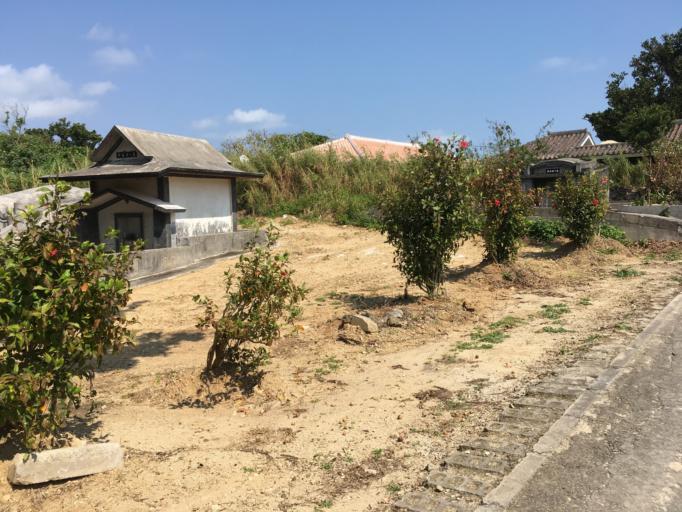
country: JP
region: Okinawa
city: Ishigaki
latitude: 24.3315
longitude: 124.0809
